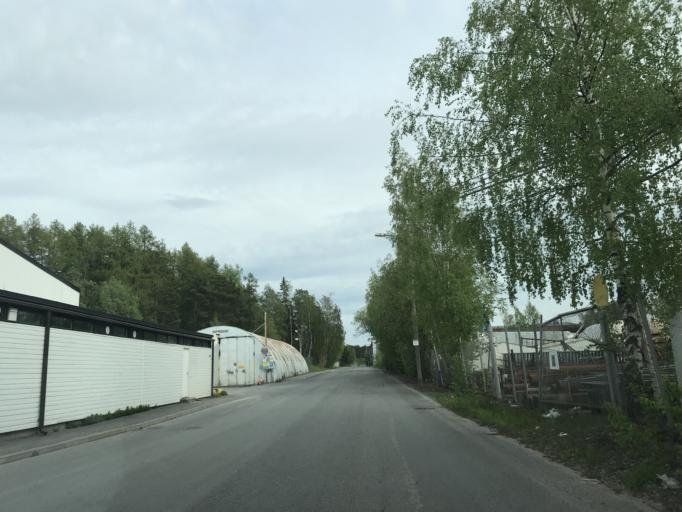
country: FI
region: Varsinais-Suomi
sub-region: Turku
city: Turku
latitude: 60.4473
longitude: 22.3080
